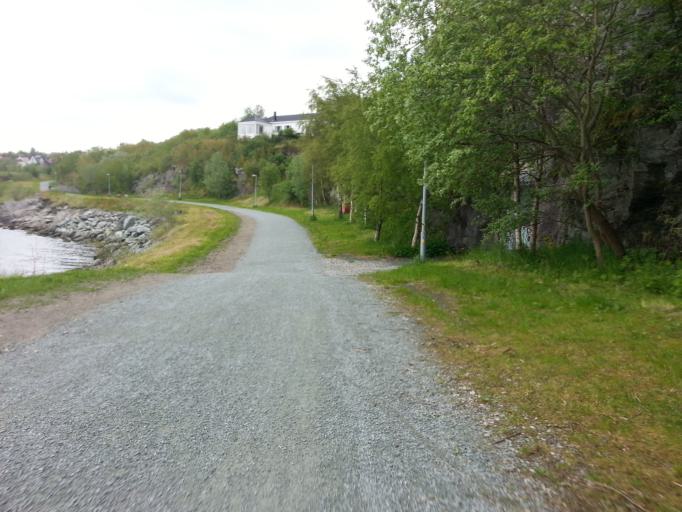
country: NO
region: Sor-Trondelag
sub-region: Trondheim
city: Trondheim
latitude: 63.4484
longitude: 10.4276
